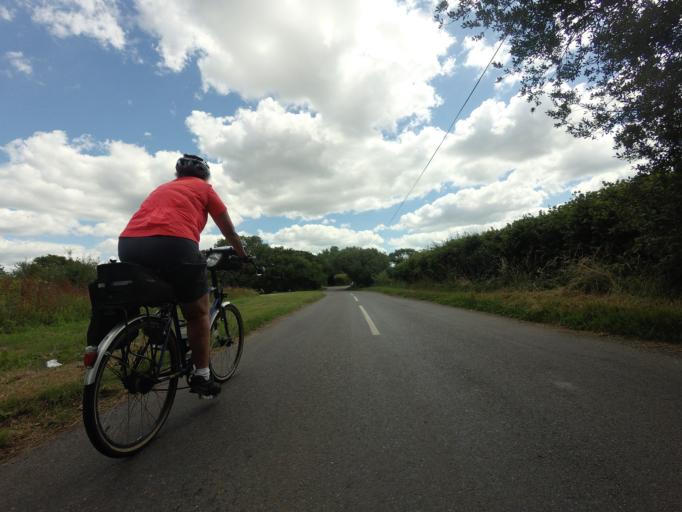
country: GB
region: England
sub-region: East Sussex
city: Hailsham
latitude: 50.8395
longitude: 0.1851
